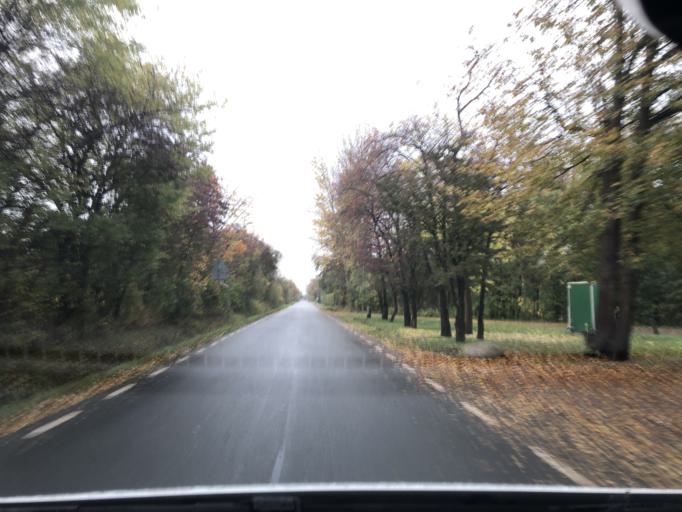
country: DK
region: Capital Region
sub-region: Tarnby Kommune
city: Tarnby
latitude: 55.5681
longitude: 12.6047
